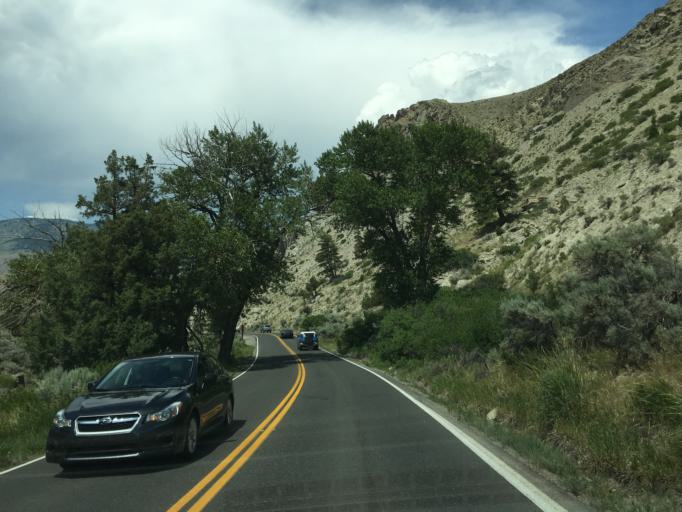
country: US
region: Montana
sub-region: Gallatin County
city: West Yellowstone
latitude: 45.0090
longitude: -110.6941
